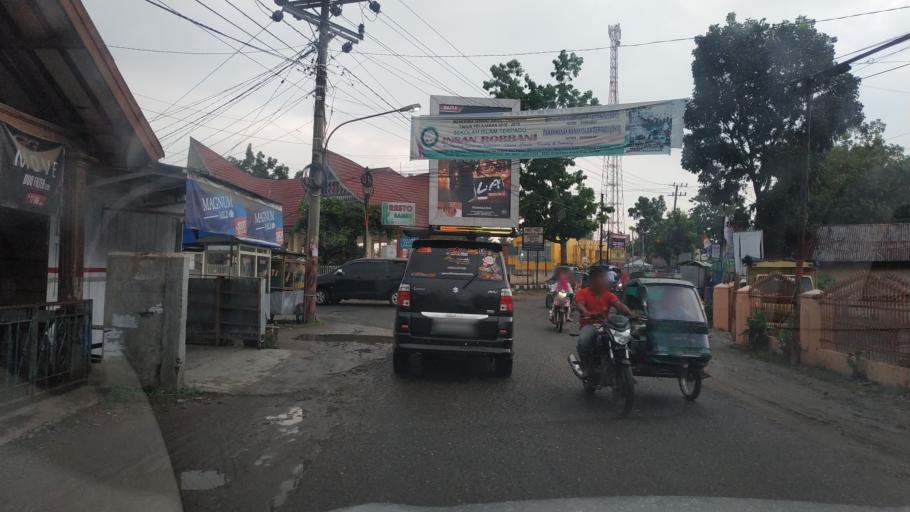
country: ID
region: North Sumatra
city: Sibubuhan
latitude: 1.0527
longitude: 99.7310
